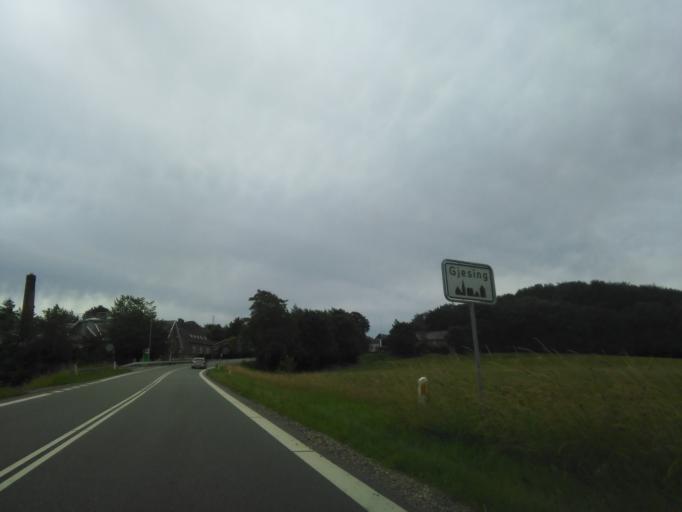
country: DK
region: Central Jutland
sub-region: Skanderborg Kommune
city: Stilling
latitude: 55.9903
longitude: 10.0230
